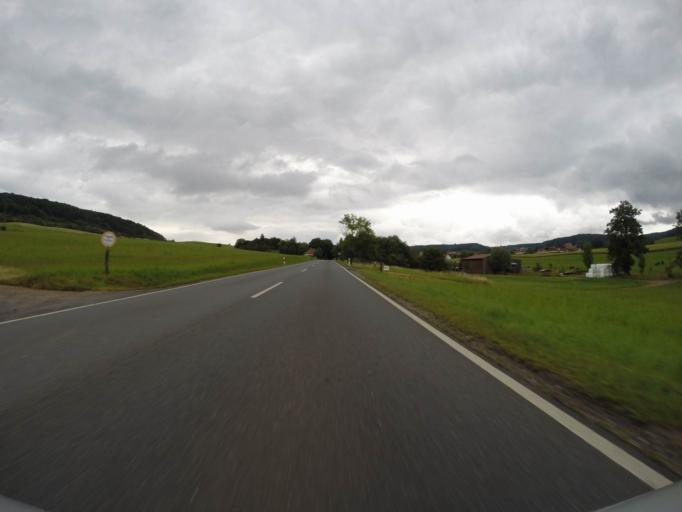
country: DE
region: Thuringia
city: Grosslobichau
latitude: 50.9318
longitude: 11.6711
